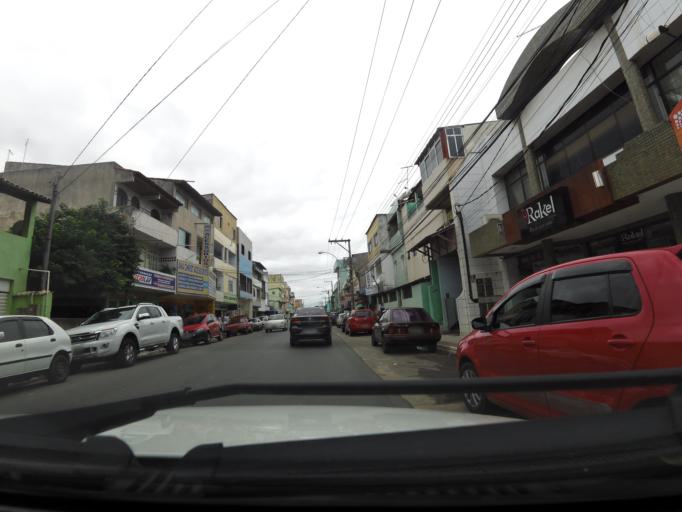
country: BR
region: Espirito Santo
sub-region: Guarapari
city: Guarapari
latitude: -20.6025
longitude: -40.4640
